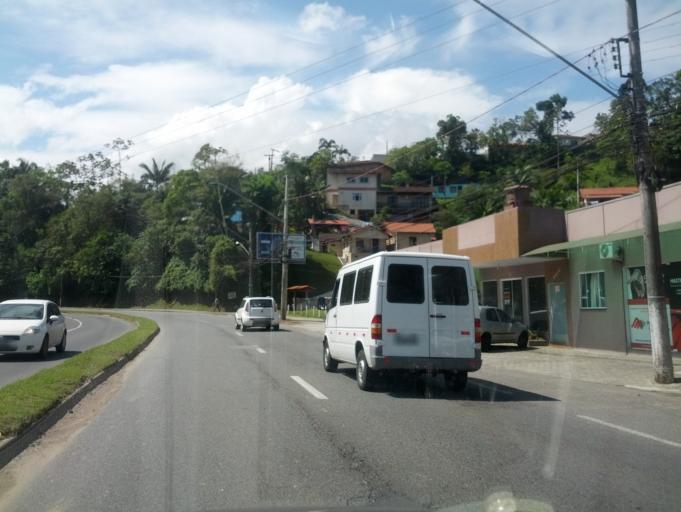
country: BR
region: Santa Catarina
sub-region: Blumenau
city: Blumenau
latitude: -26.8959
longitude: -49.0582
